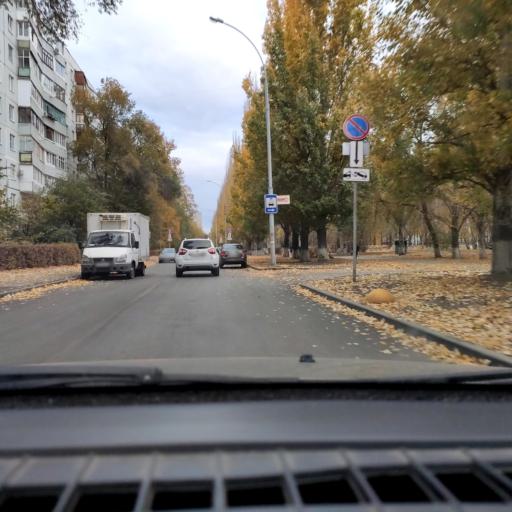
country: RU
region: Samara
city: Tol'yatti
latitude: 53.5220
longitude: 49.3016
